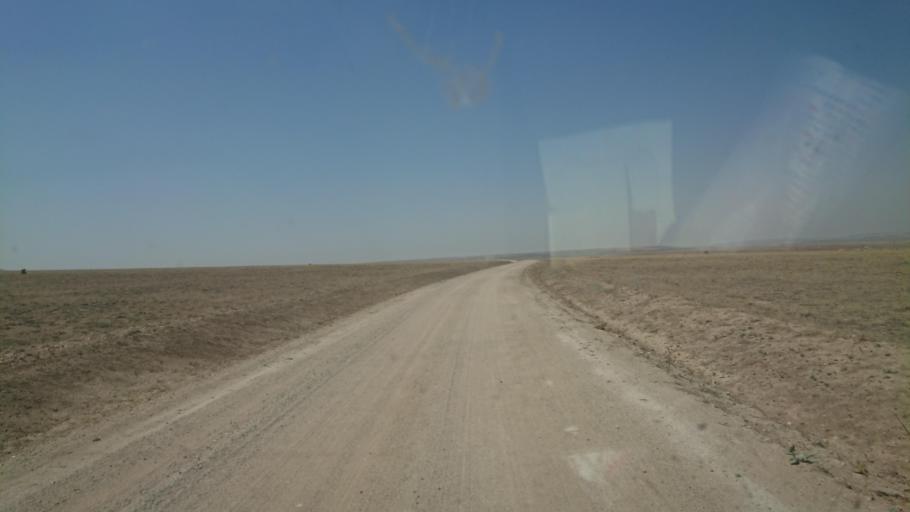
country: TR
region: Aksaray
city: Agacoren
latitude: 38.7470
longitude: 33.9009
